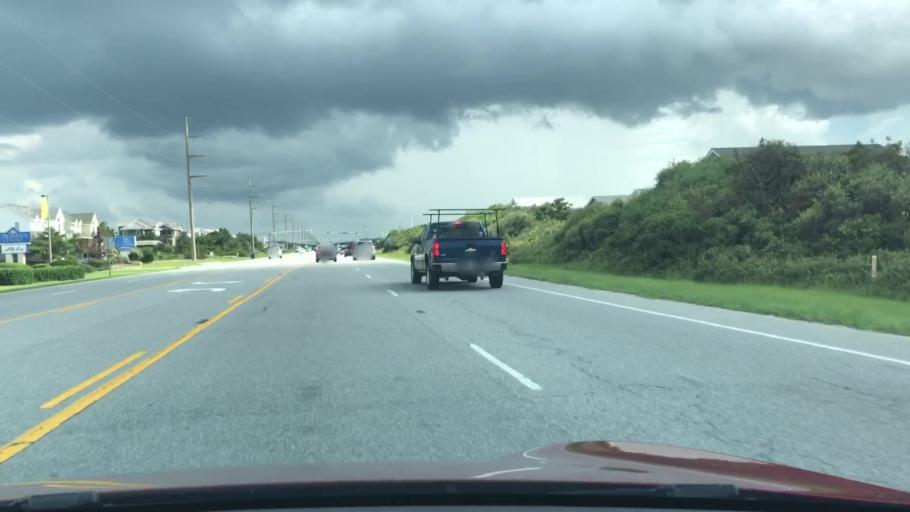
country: US
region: North Carolina
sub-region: Dare County
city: Nags Head
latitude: 35.9423
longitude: -75.6185
